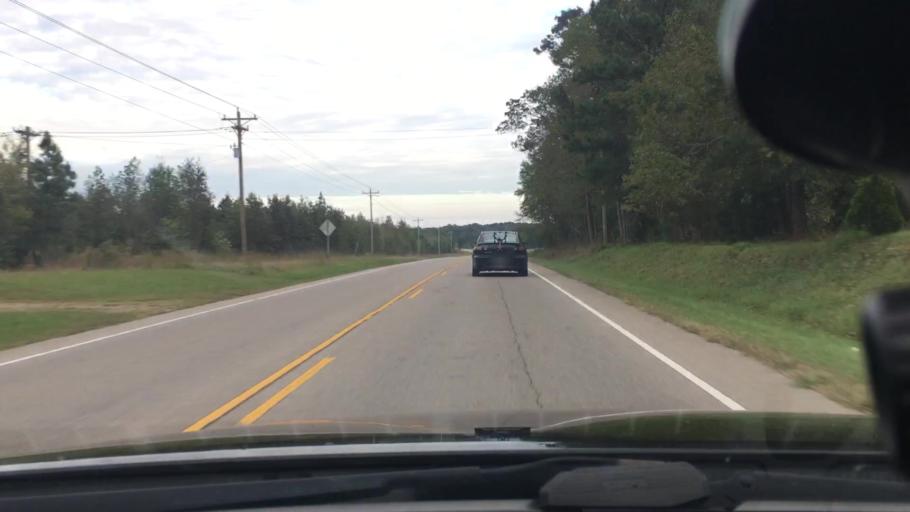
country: US
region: North Carolina
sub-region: Moore County
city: Robbins
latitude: 35.4006
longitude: -79.5530
